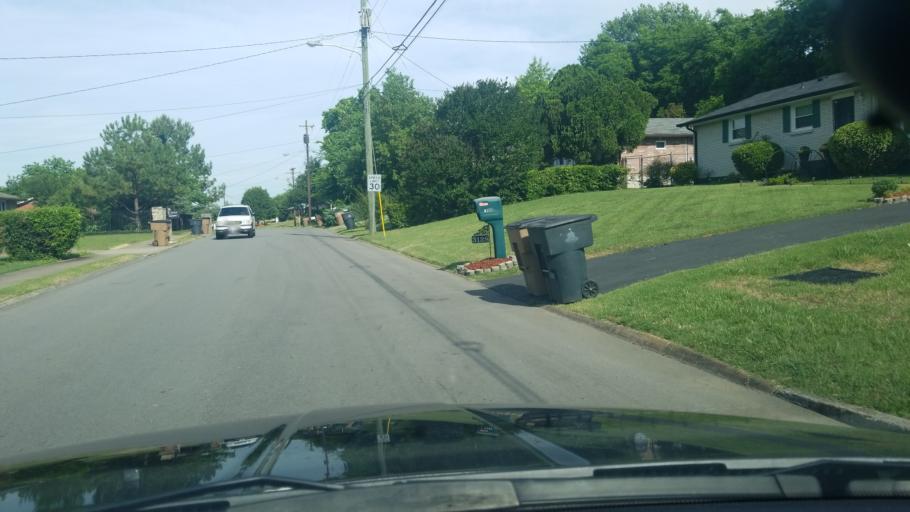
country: US
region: Tennessee
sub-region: Davidson County
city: Nashville
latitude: 36.2356
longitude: -86.7787
